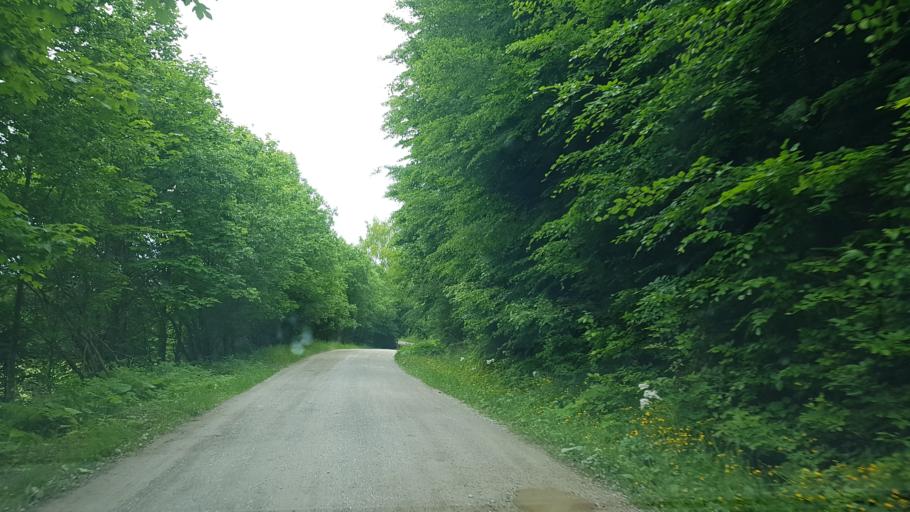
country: SI
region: Dobrna
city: Dobrna
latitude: 46.3826
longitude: 15.2327
